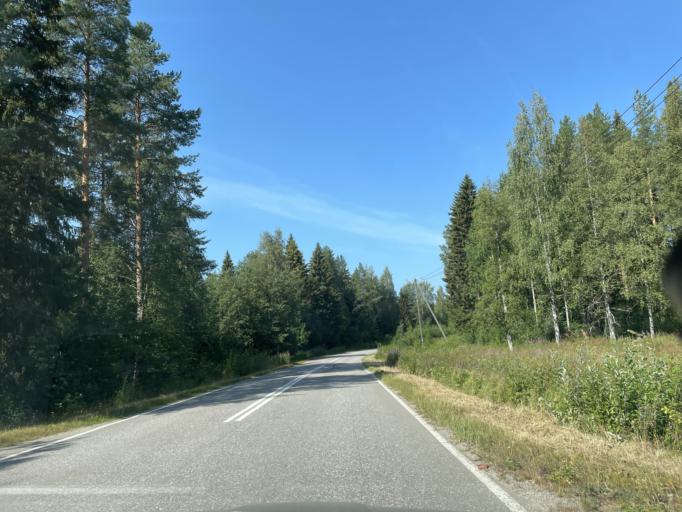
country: FI
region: Central Finland
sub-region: Saarijaervi-Viitasaari
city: Pihtipudas
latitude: 63.3551
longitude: 25.7614
